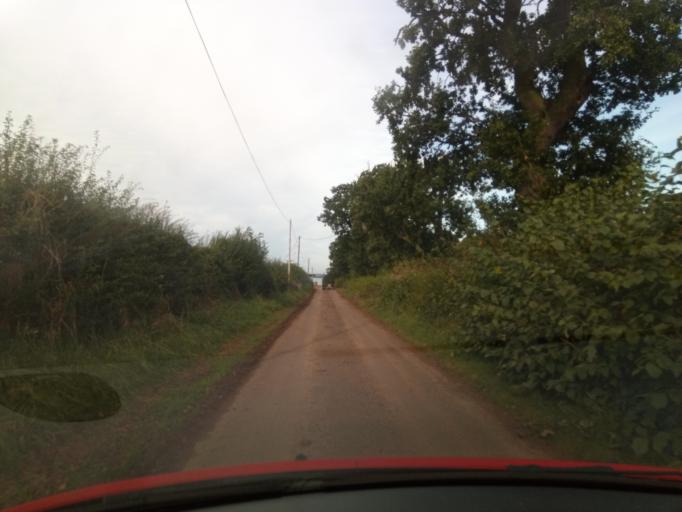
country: GB
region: Scotland
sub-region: The Scottish Borders
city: Kelso
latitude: 55.5933
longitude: -2.3885
